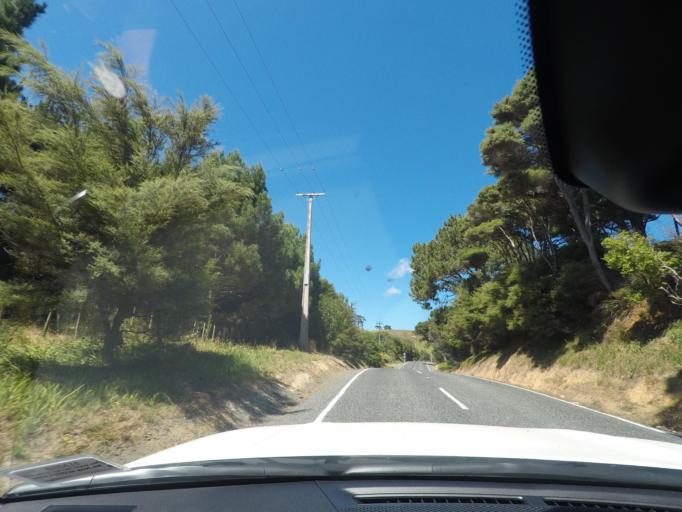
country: NZ
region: Auckland
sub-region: Auckland
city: Parakai
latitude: -36.5817
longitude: 174.3340
